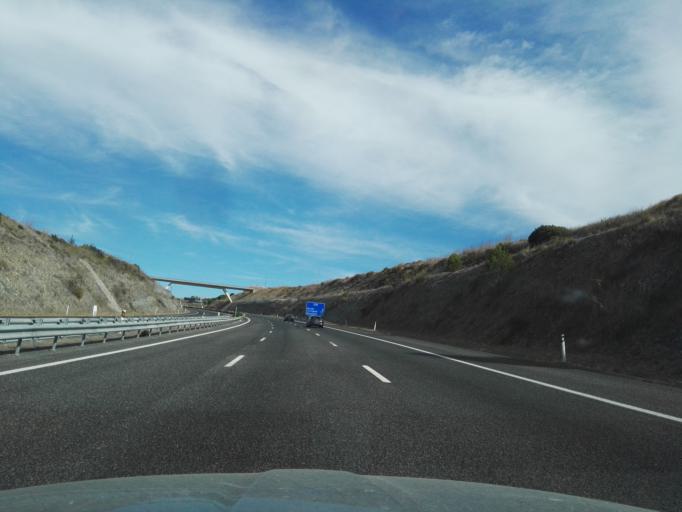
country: PT
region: Lisbon
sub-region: Vila Franca de Xira
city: Vialonga
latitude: 38.9149
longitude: -9.0725
